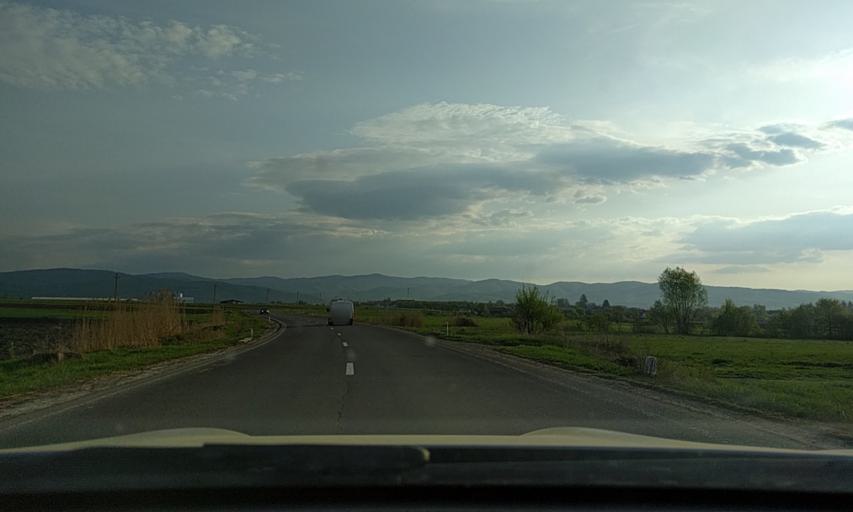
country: RO
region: Covasna
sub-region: Comuna Lemnia
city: Lemnia
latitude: 46.0422
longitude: 26.2507
